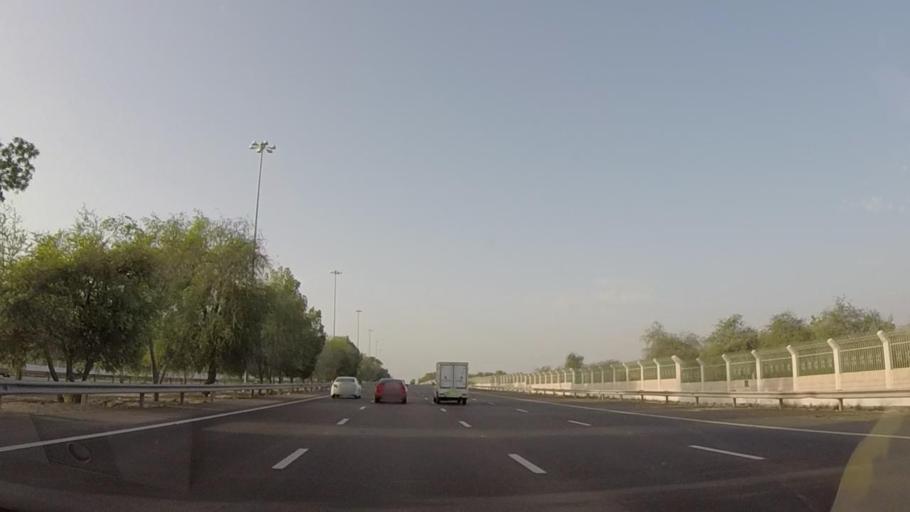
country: AE
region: Dubai
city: Dubai
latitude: 24.8307
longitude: 54.8828
